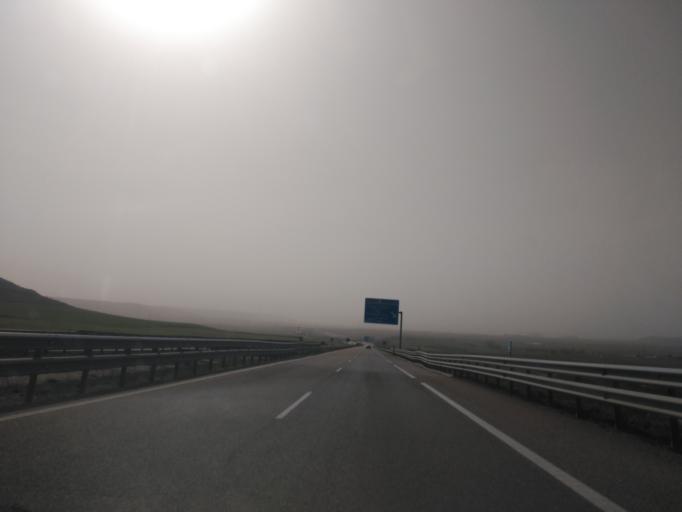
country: ES
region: Castille and Leon
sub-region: Provincia de Palencia
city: Fuentes de Valdepero
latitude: 42.0841
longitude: -4.4890
